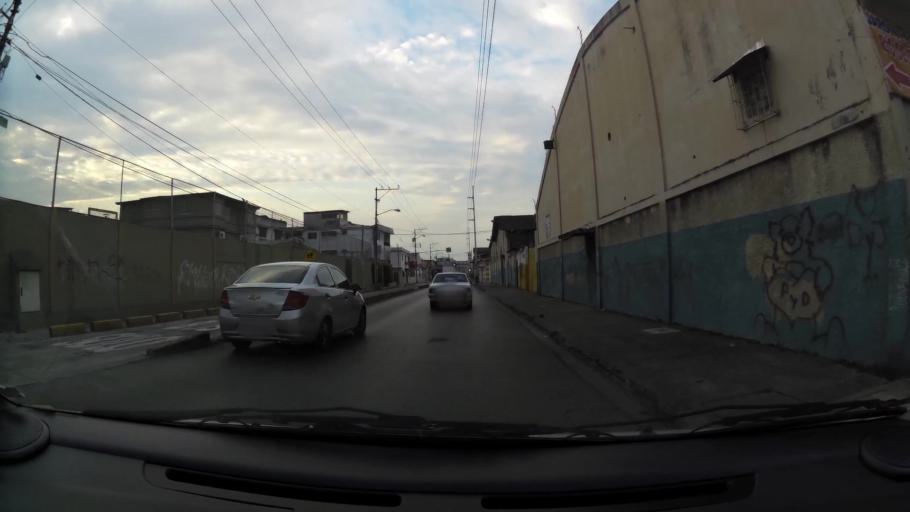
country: EC
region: Guayas
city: Guayaquil
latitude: -2.2240
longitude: -79.8894
